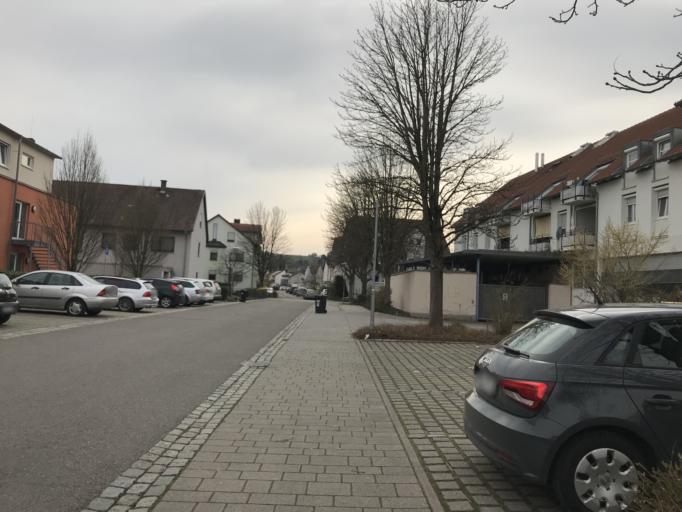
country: DE
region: Baden-Wuerttemberg
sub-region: Regierungsbezirk Stuttgart
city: Unterensingen
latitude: 48.6558
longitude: 9.3573
